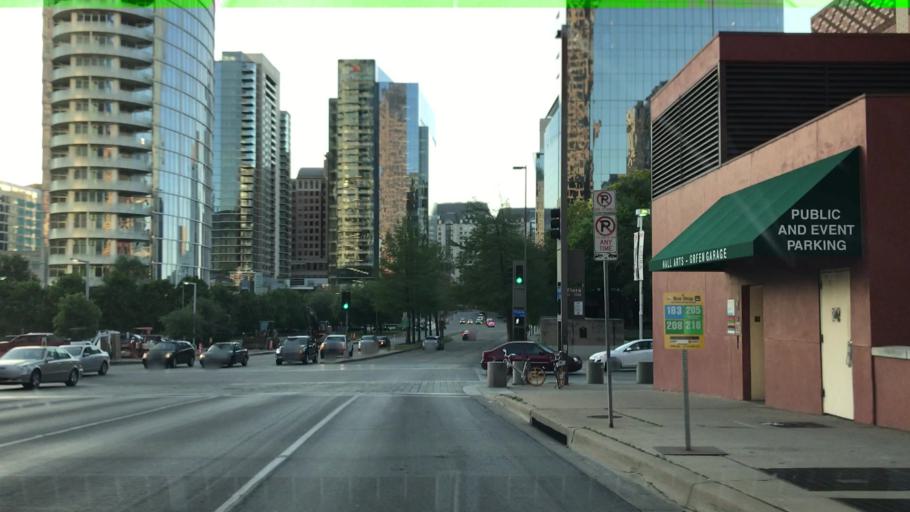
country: US
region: Texas
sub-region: Dallas County
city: Dallas
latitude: 32.7888
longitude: -96.7984
